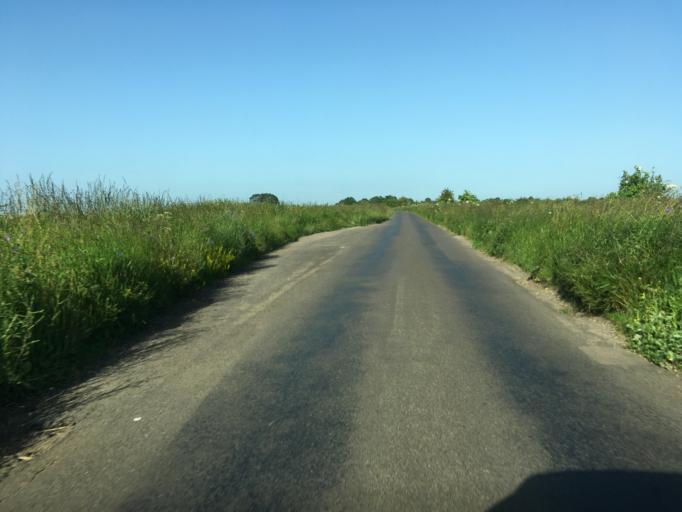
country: GB
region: England
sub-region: Oxfordshire
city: Shipton under Wychwood
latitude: 51.8355
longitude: -1.6173
